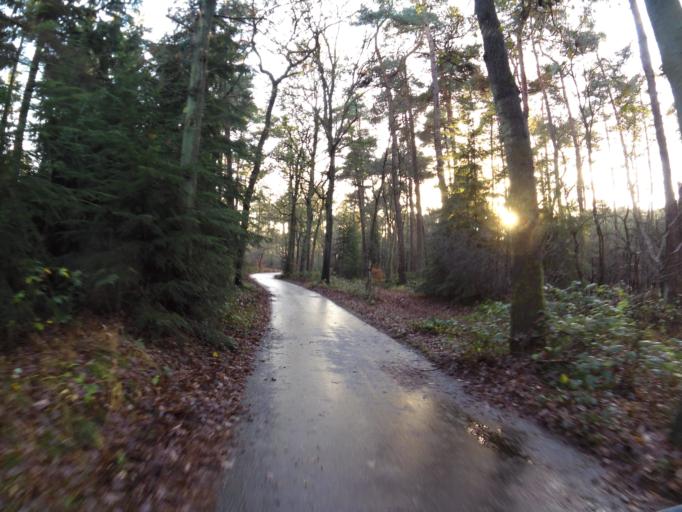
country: NL
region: North Brabant
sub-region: Gemeente Waalwijk
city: Waalwijk
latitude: 51.6600
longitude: 5.0968
